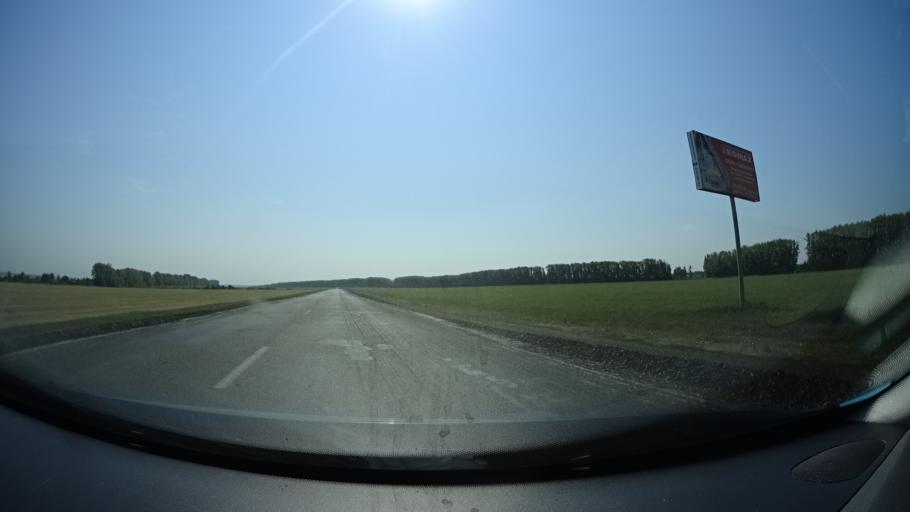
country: RU
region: Bashkortostan
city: Kabakovo
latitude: 54.4608
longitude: 55.9646
